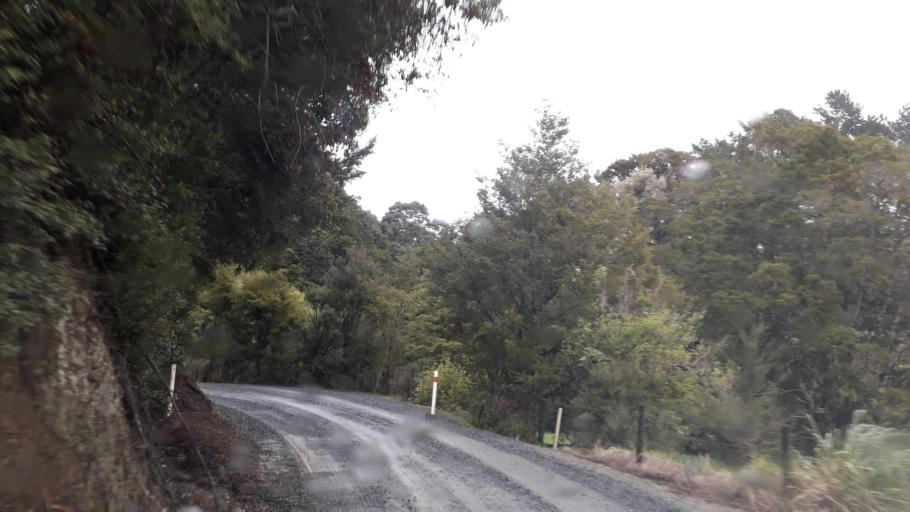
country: NZ
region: Northland
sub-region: Far North District
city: Waimate North
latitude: -35.1324
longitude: 173.7184
